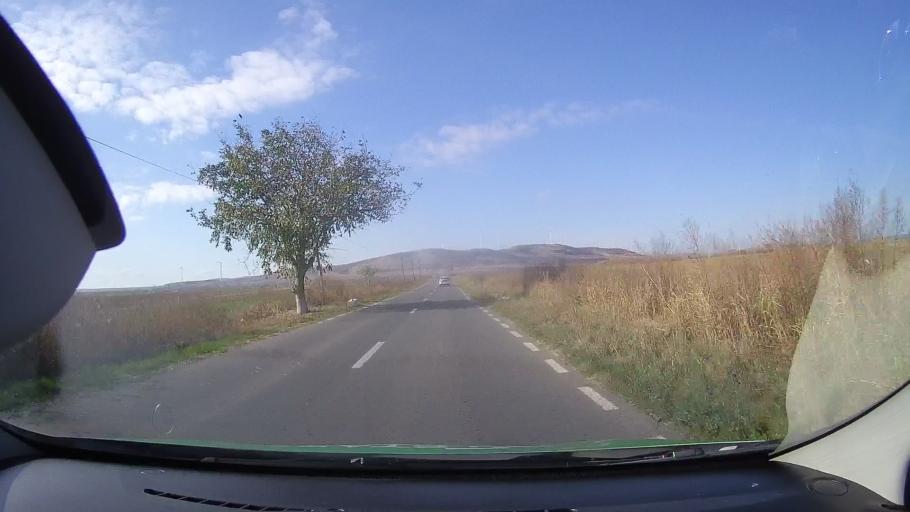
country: RO
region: Tulcea
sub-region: Comuna Valea Nucarilor
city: Agighiol
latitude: 45.0355
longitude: 28.8942
